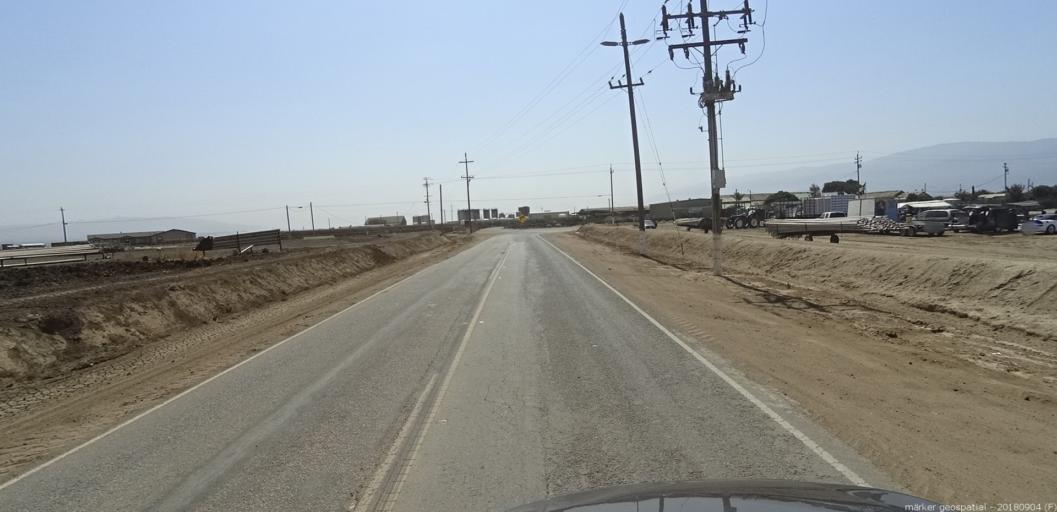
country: US
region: California
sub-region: Monterey County
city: Gonzales
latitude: 36.5378
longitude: -121.4633
